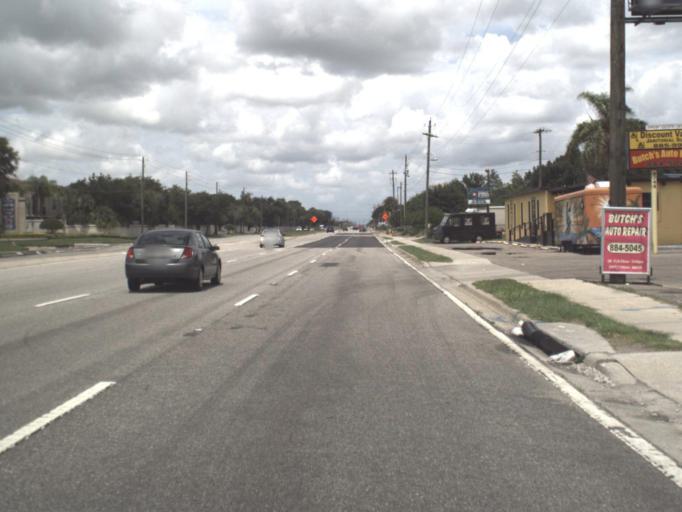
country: US
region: Florida
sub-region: Hillsborough County
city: Town 'n' Country
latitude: 28.0019
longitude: -82.5946
